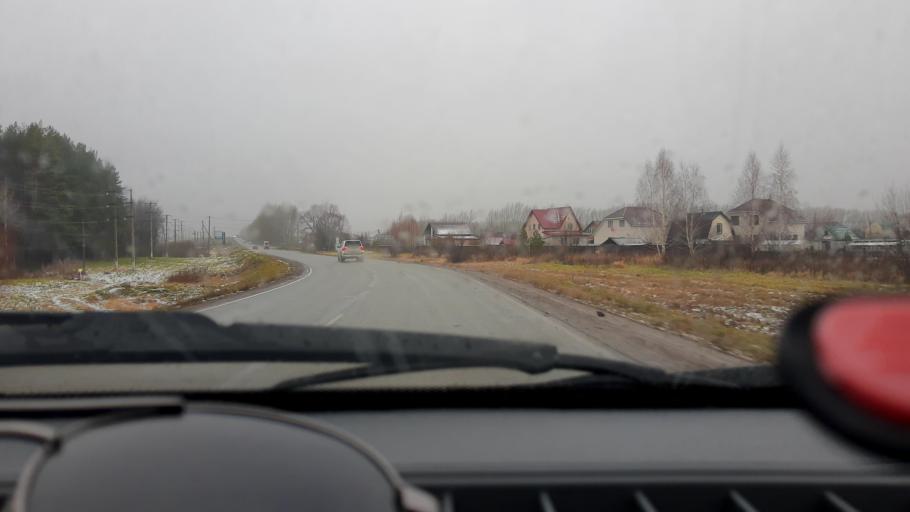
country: RU
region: Bashkortostan
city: Kabakovo
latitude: 54.6126
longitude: 56.1646
